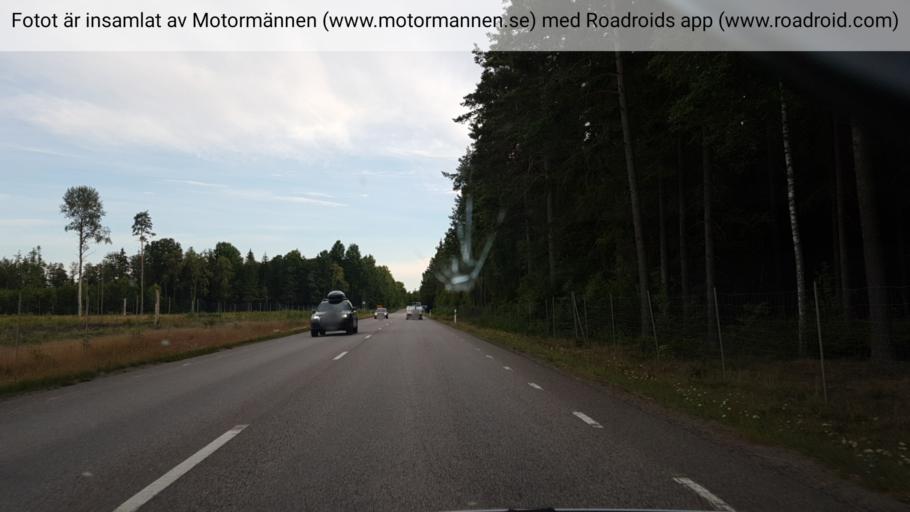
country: SE
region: Vaestra Goetaland
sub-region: Tibro Kommun
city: Tibro
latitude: 58.4387
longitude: 14.1772
